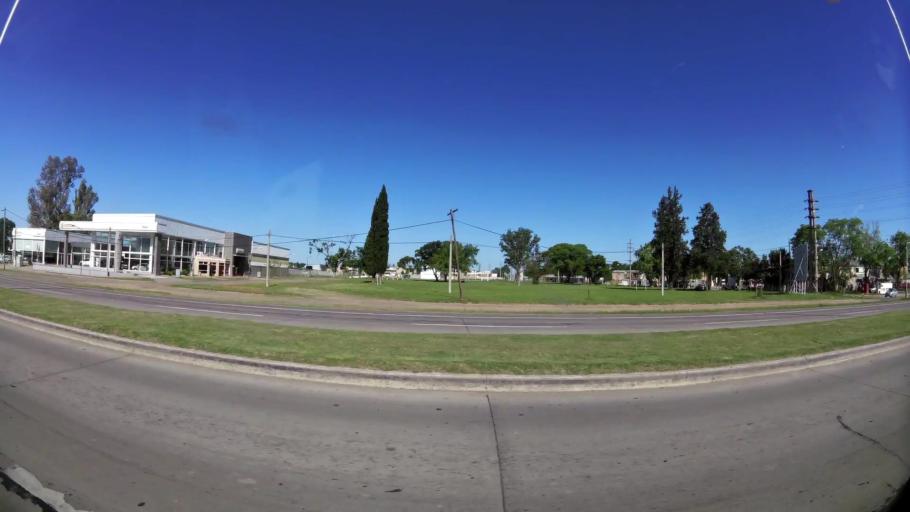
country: AR
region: Santa Fe
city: Rafaela
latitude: -31.2672
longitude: -61.5090
